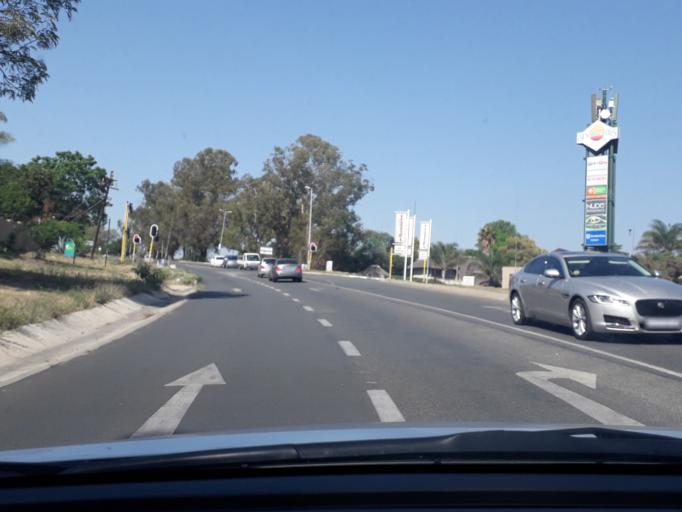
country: ZA
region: Gauteng
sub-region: City of Johannesburg Metropolitan Municipality
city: Roodepoort
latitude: -26.0859
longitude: 27.9478
